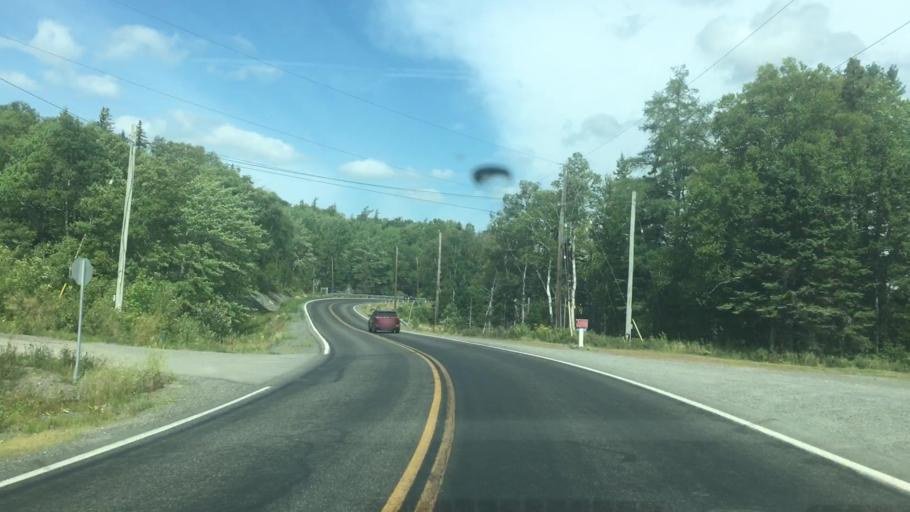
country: CA
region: Nova Scotia
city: Sydney Mines
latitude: 46.2129
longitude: -60.6198
